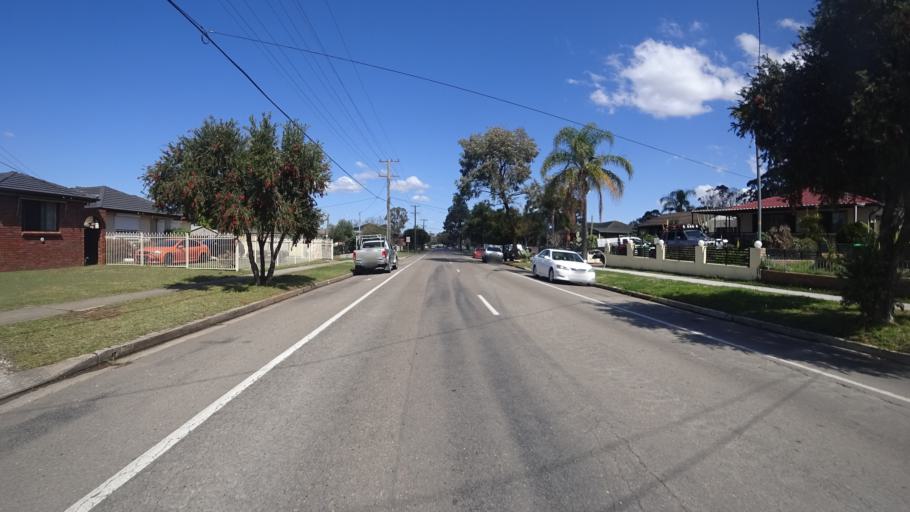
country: AU
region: New South Wales
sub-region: Liverpool
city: Miller
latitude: -33.9134
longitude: 150.8950
